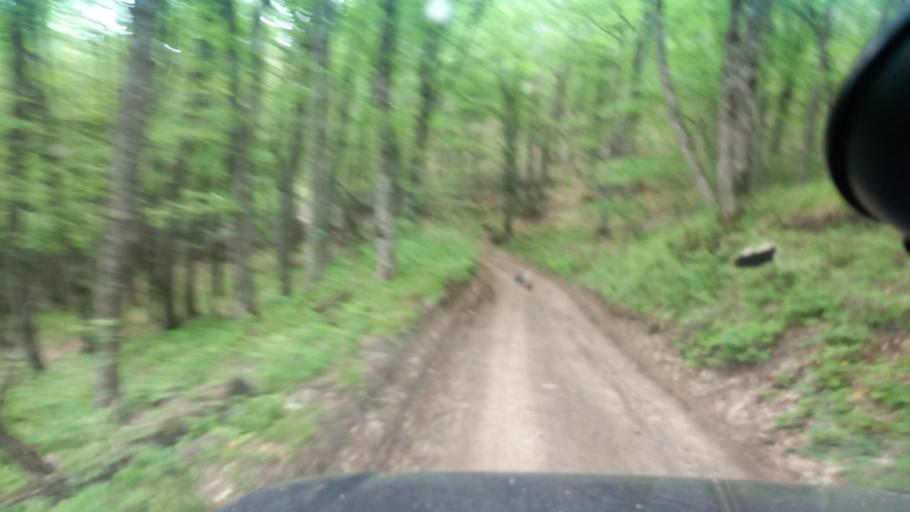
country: RU
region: Krasnodarskiy
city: Tuapse
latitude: 44.2504
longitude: 39.2818
